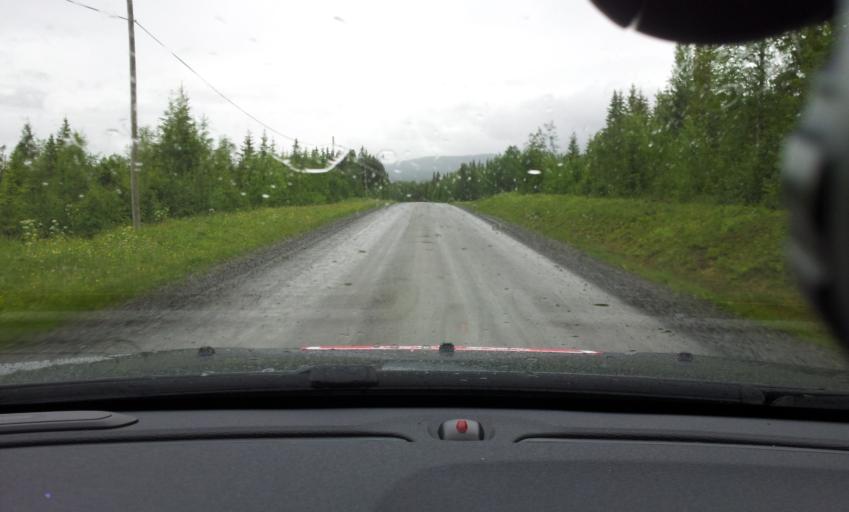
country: SE
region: Jaemtland
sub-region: Are Kommun
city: Are
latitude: 63.4383
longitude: 12.8073
